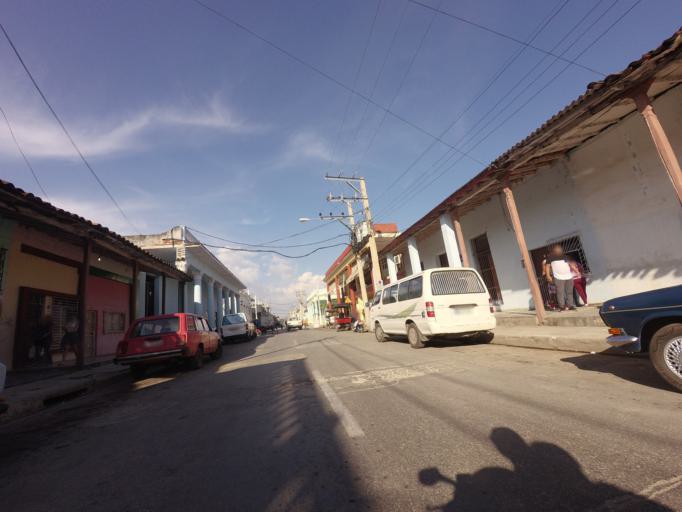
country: CU
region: Ciego de Avila
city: Ciego de Avila
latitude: 21.8422
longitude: -78.7634
